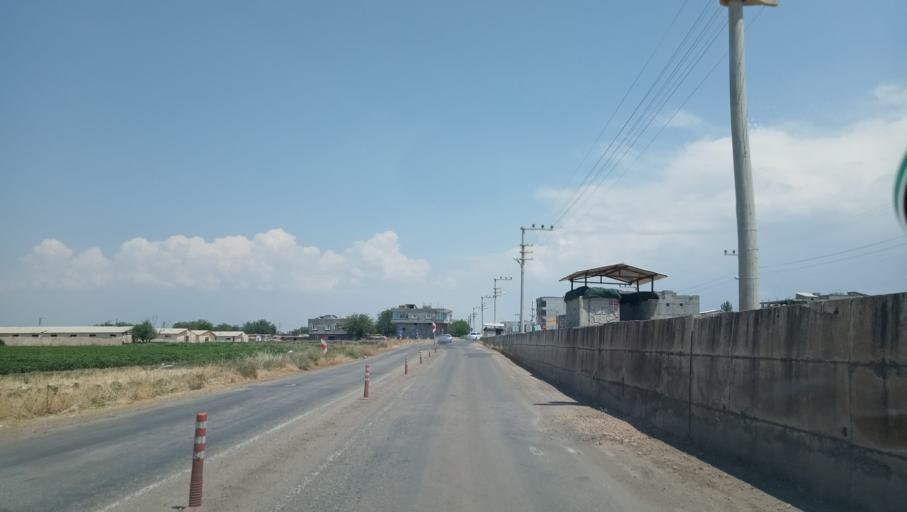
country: TR
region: Diyarbakir
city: Tepe
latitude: 37.7932
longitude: 40.7606
